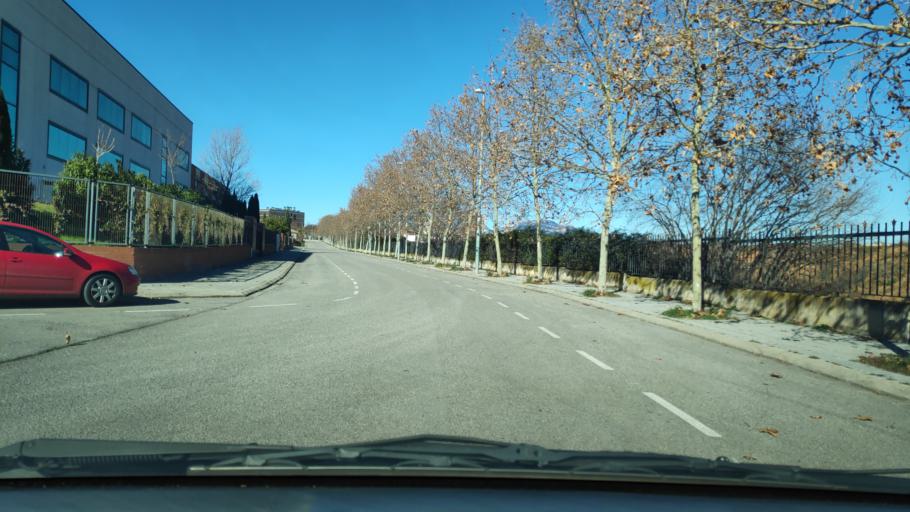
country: ES
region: Catalonia
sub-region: Provincia de Barcelona
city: Sant Quirze del Valles
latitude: 41.5375
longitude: 2.0935
